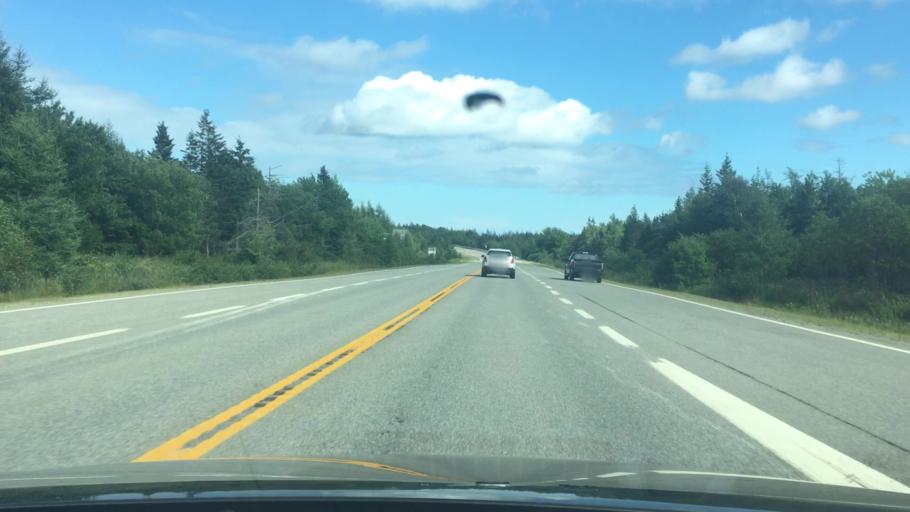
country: CA
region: Nova Scotia
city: Princeville
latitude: 45.6120
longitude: -61.0766
